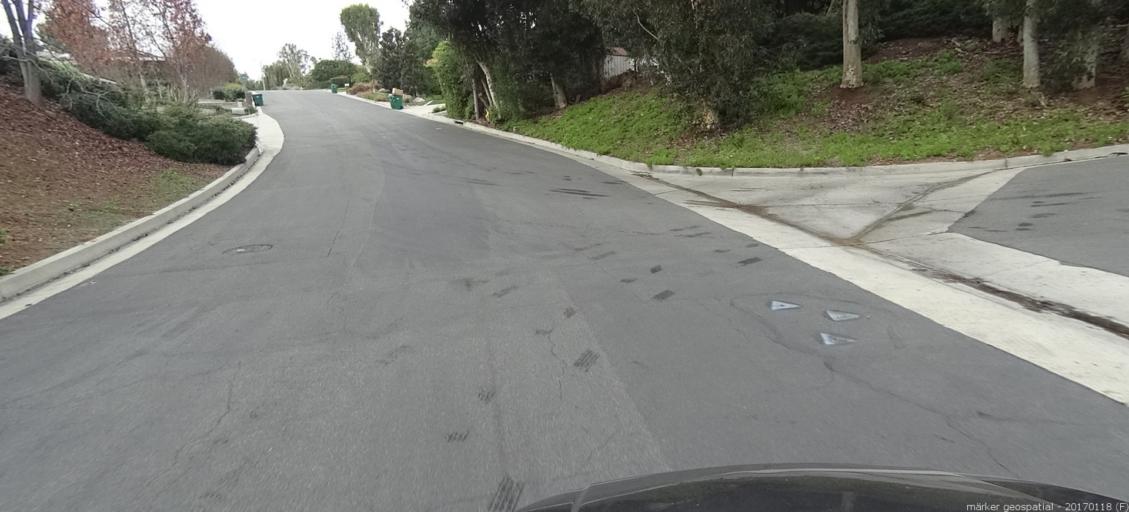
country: US
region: California
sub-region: Orange County
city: North Tustin
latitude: 33.7534
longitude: -117.7810
